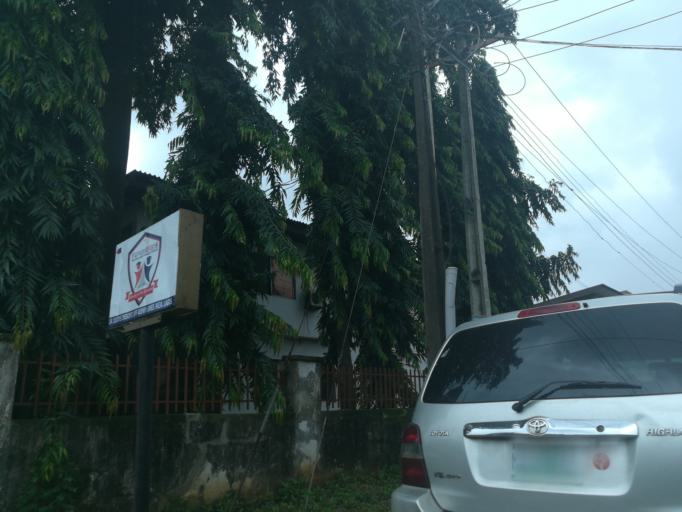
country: NG
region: Lagos
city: Agege
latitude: 6.6186
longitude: 3.3441
